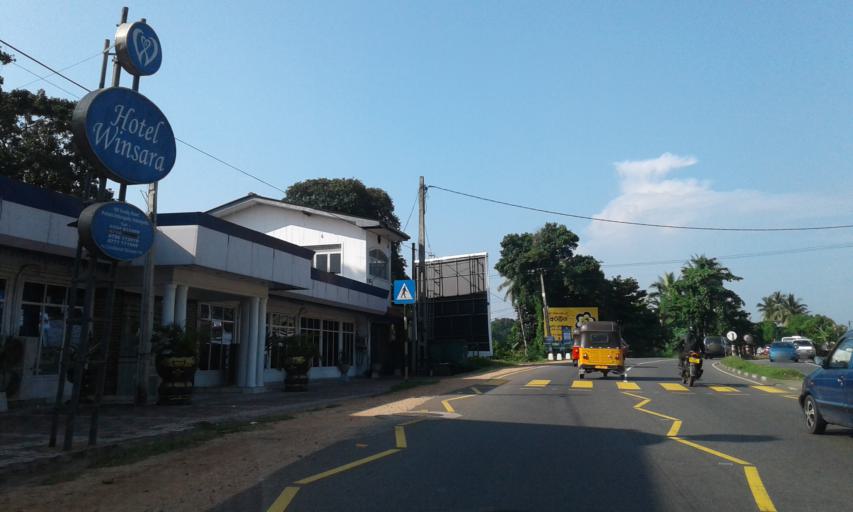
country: LK
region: Western
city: Gampaha
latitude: 7.0435
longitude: 79.9963
